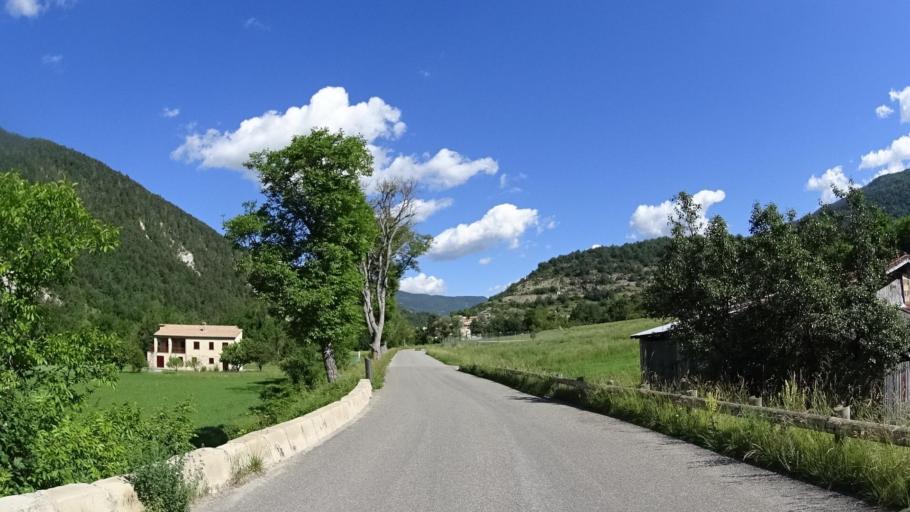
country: FR
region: Provence-Alpes-Cote d'Azur
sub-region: Departement des Alpes-de-Haute-Provence
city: Annot
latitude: 43.9989
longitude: 6.6446
